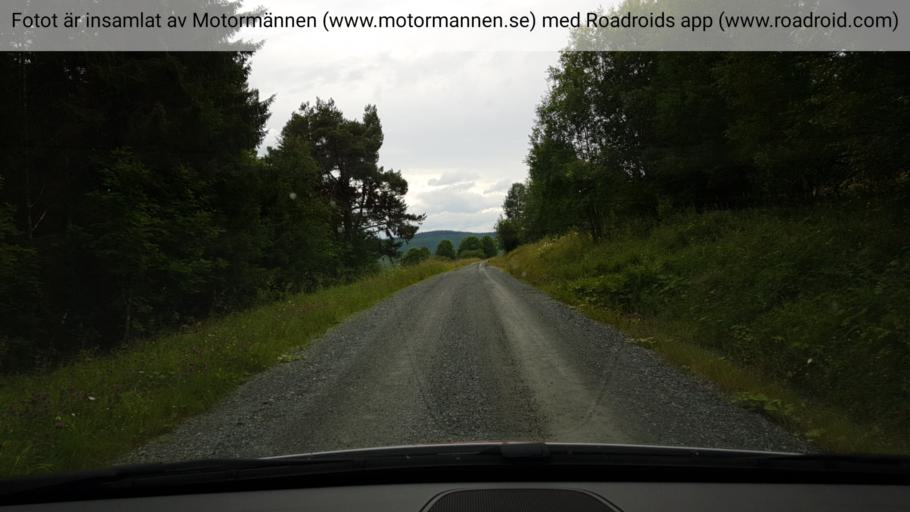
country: SE
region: Jaemtland
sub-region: Krokoms Kommun
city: Valla
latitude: 63.5856
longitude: 13.9954
